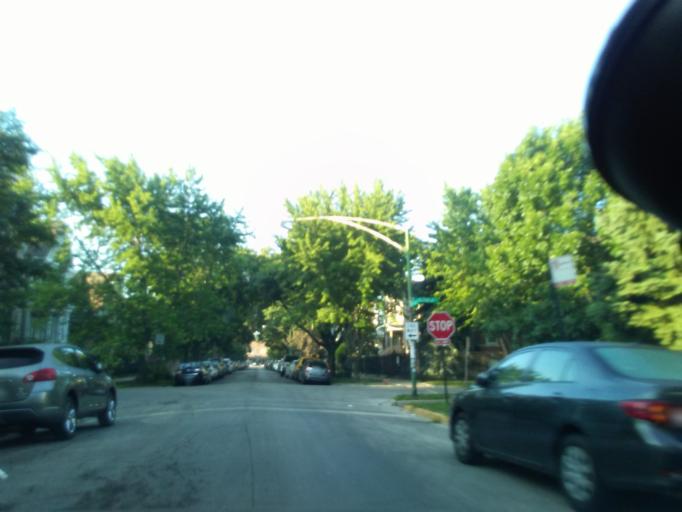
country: US
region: Illinois
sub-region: Cook County
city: Lincolnwood
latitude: 41.9267
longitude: -87.7158
